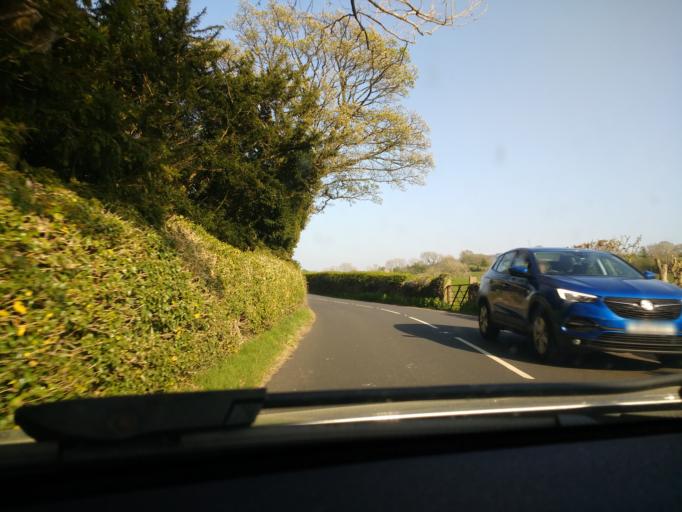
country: GB
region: England
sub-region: Cumbria
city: Sedbergh
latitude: 54.3201
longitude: -2.4988
